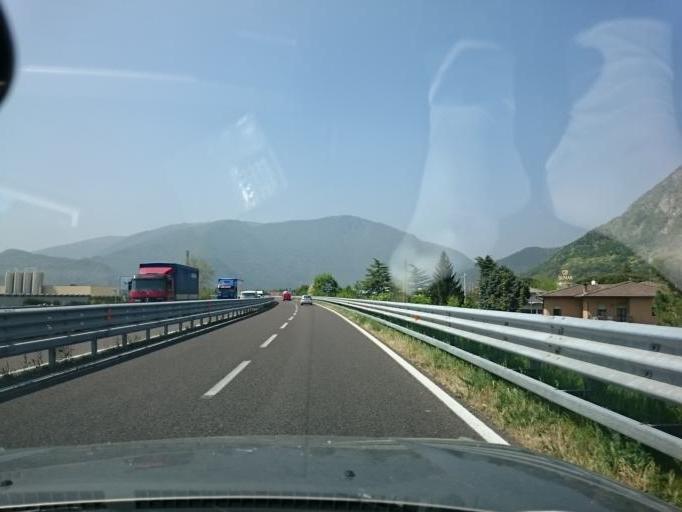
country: IT
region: Veneto
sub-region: Provincia di Vicenza
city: Romano d'Ezzelino
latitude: 45.7878
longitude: 11.7490
